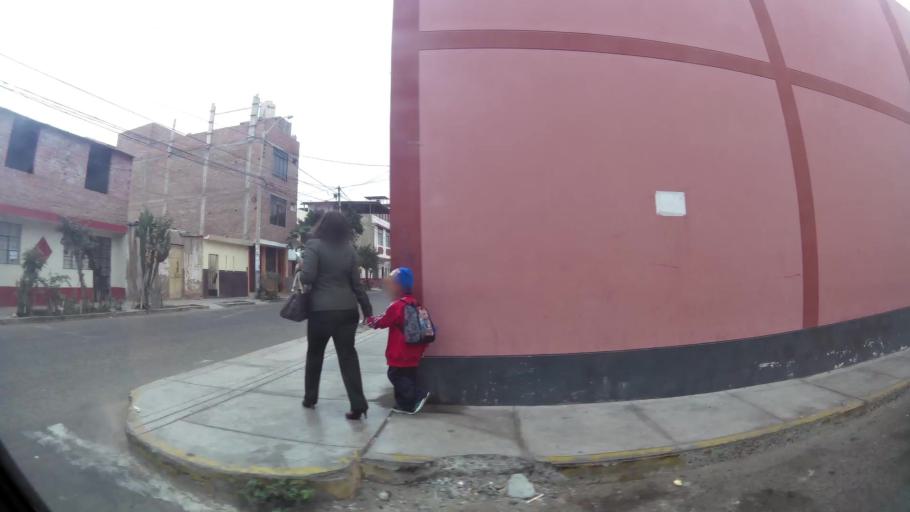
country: PE
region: La Libertad
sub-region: Provincia de Trujillo
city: Trujillo
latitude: -8.1040
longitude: -79.0400
